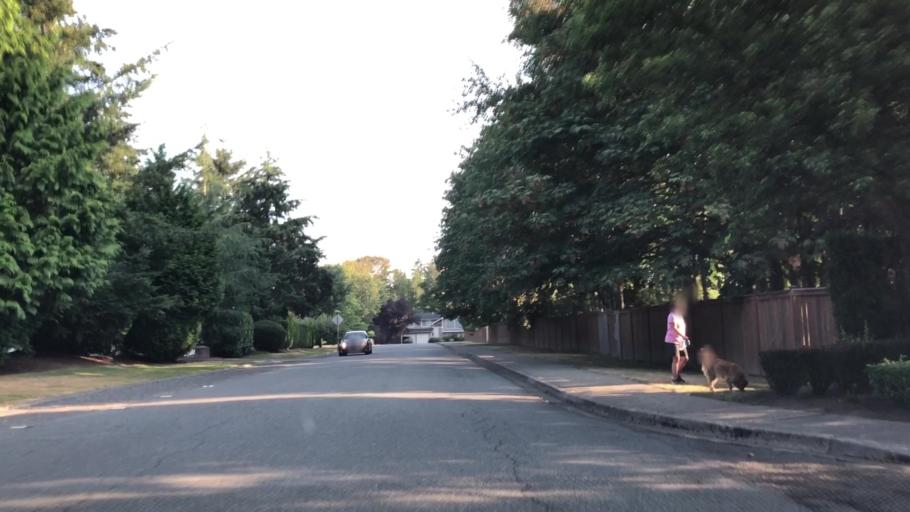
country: US
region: Washington
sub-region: King County
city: Cottage Lake
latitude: 47.7202
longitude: -122.1021
